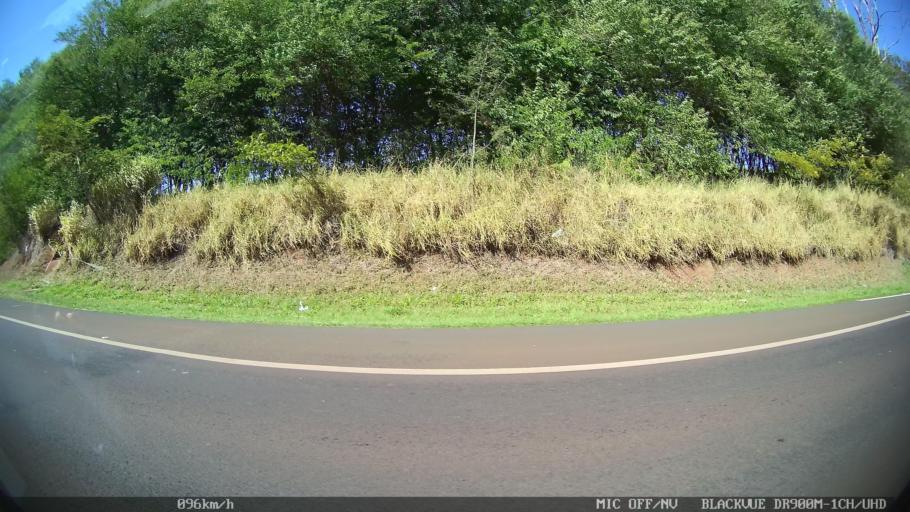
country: BR
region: Sao Paulo
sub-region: Franca
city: Franca
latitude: -20.5849
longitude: -47.4327
